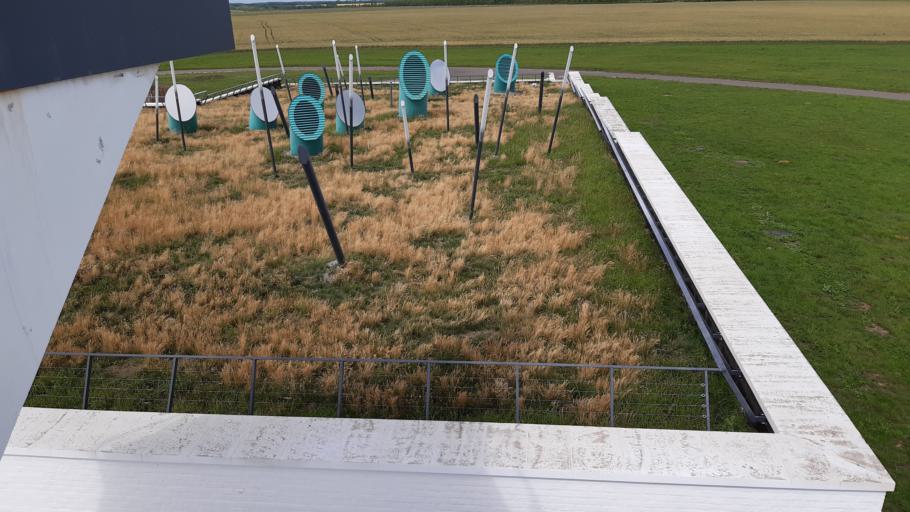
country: RU
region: Tula
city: Kurkino
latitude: 53.6249
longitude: 38.6727
